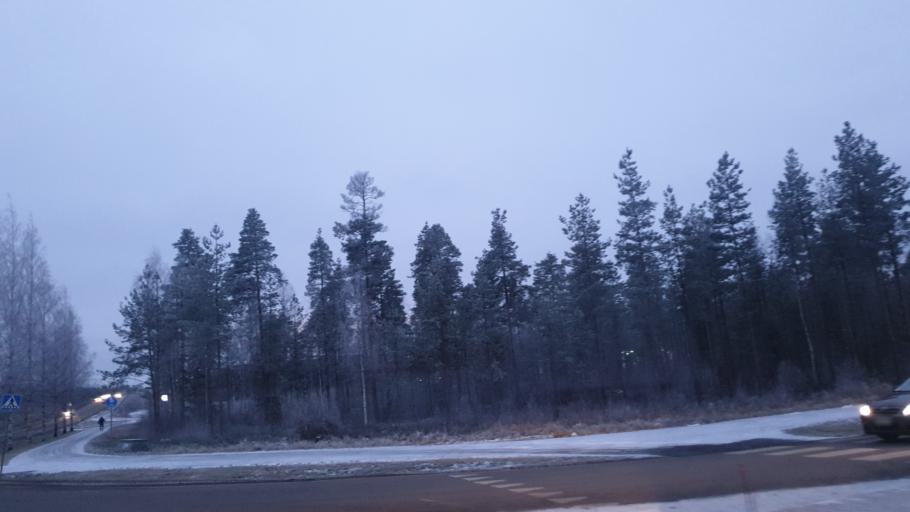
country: FI
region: Southern Ostrobothnia
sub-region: Seinaejoki
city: Nurmo
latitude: 62.7777
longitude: 22.8938
